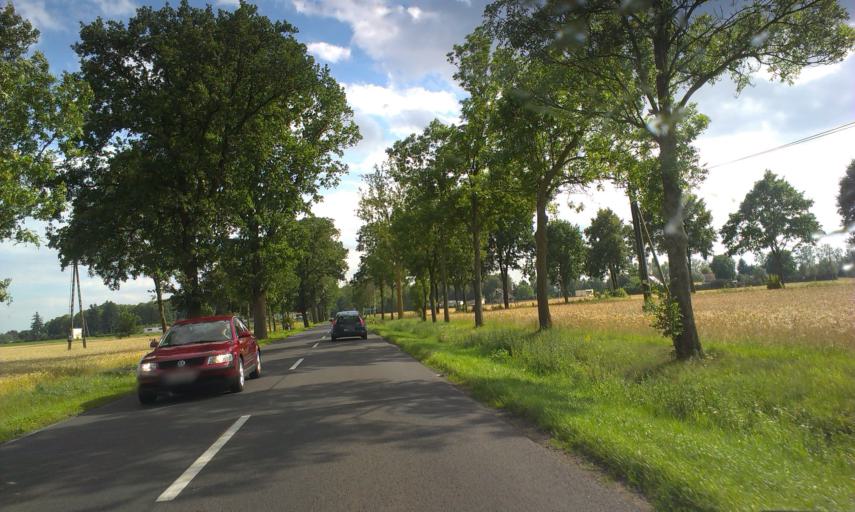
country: PL
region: Greater Poland Voivodeship
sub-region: Powiat zlotowski
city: Krajenka
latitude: 53.3078
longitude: 16.9888
